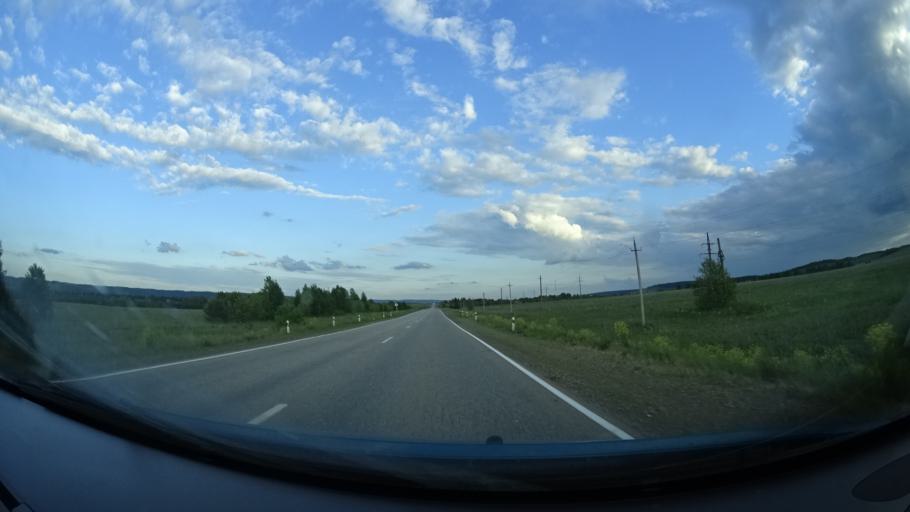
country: RU
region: Perm
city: Barda
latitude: 57.0056
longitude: 55.5651
